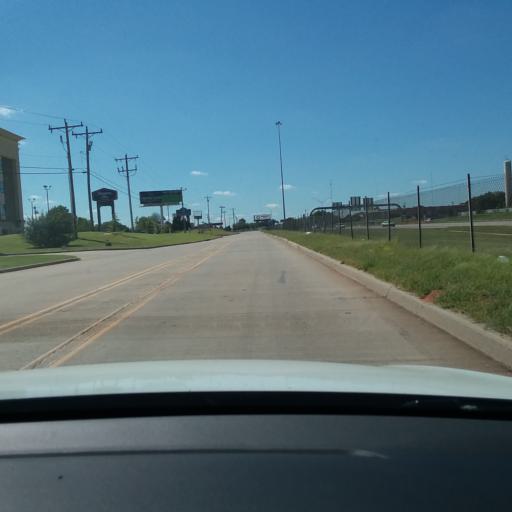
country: US
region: Oklahoma
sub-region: Oklahoma County
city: Edmond
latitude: 35.5915
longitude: -97.4335
